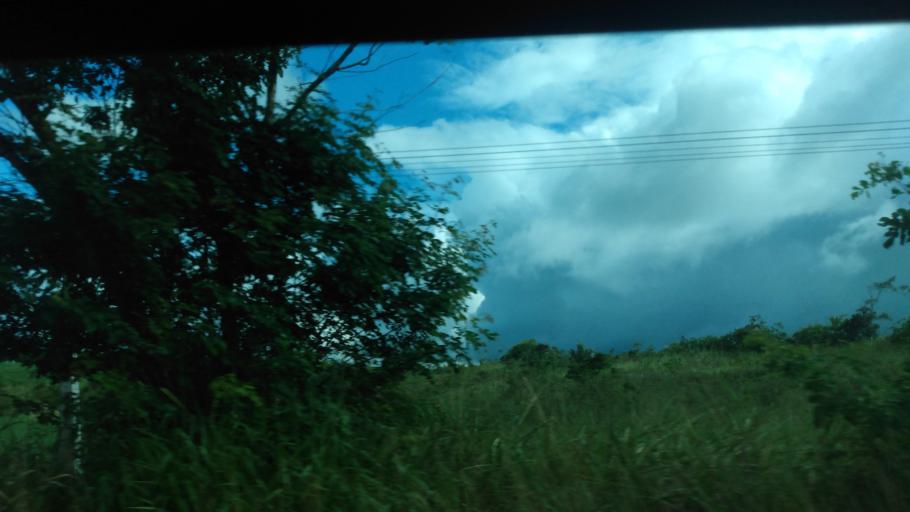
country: BR
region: Pernambuco
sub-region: Quipapa
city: Quipapa
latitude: -8.7785
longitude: -35.9403
